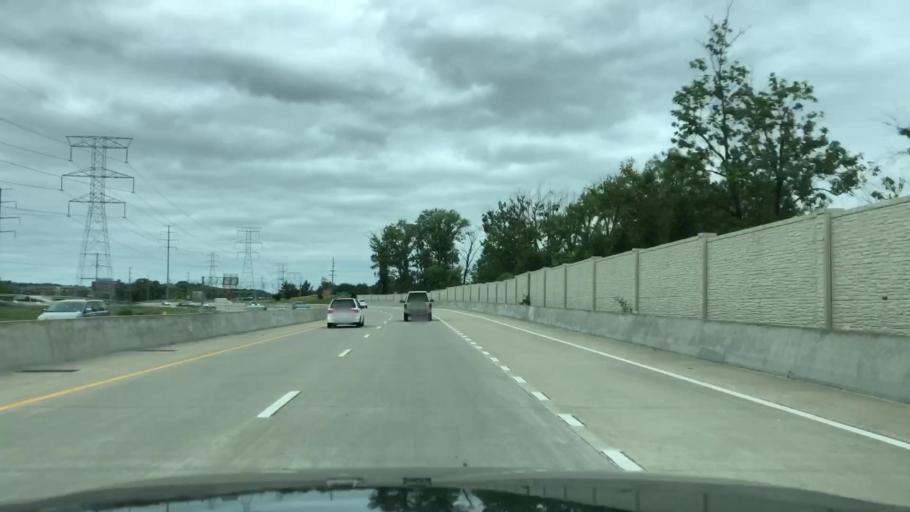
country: US
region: Missouri
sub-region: Saint Louis County
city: Town and Country
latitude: 38.6680
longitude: -90.4989
